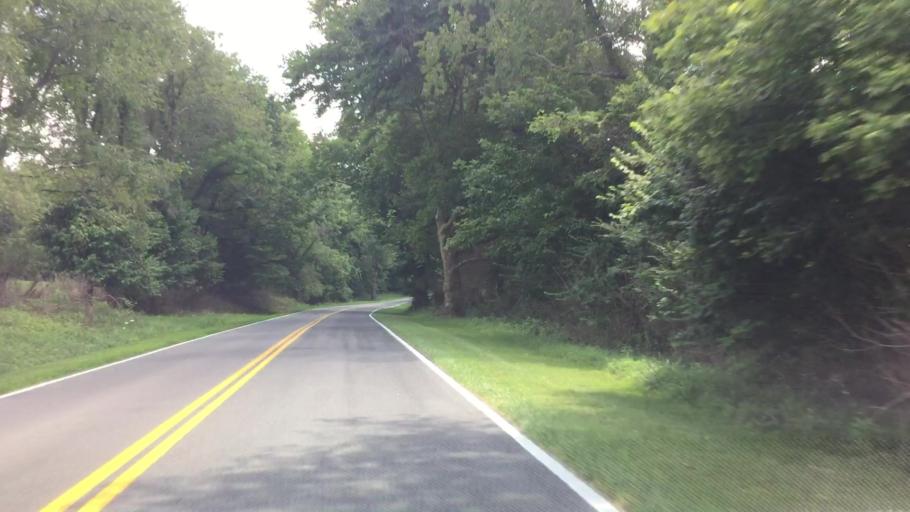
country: US
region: Virginia
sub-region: Pulaski County
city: Pulaski
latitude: 36.9981
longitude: -80.7997
